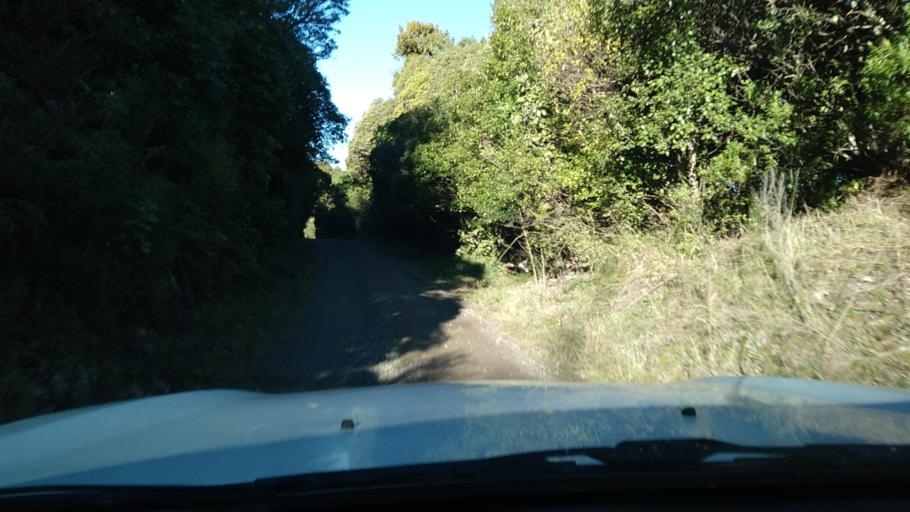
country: NZ
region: Waikato
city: Turangi
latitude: -38.6416
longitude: 175.6652
